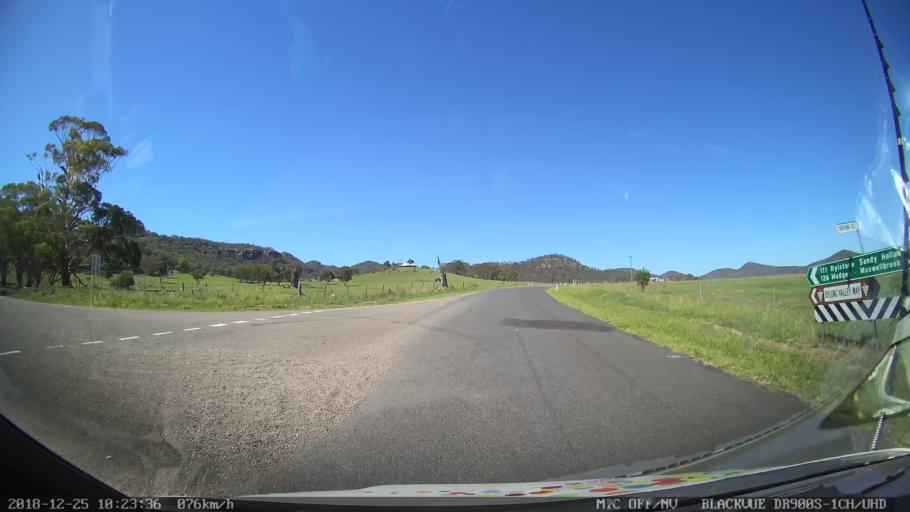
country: AU
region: New South Wales
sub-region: Muswellbrook
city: Denman
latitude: -32.3876
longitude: 150.5223
